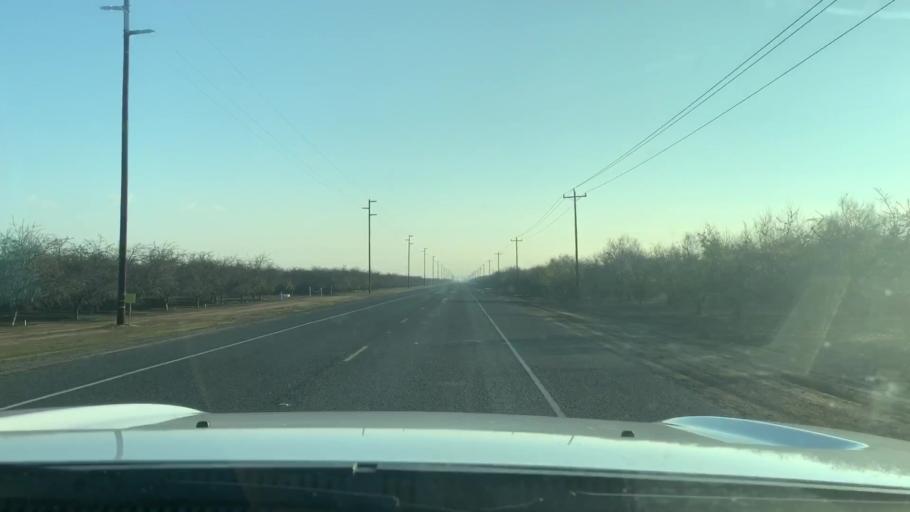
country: US
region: California
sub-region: Kern County
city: Wasco
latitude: 35.6011
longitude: -119.4703
